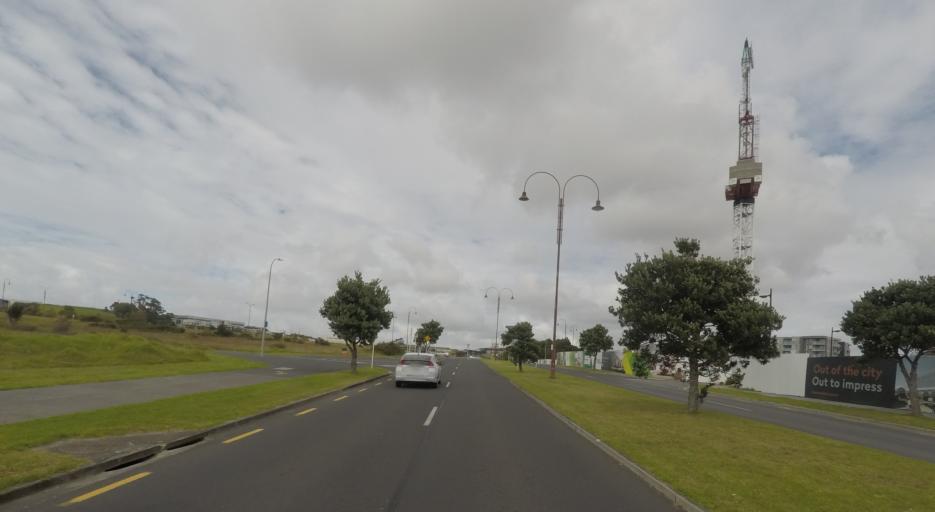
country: NZ
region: Auckland
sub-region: Auckland
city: Rothesay Bay
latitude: -36.7230
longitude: 174.7088
